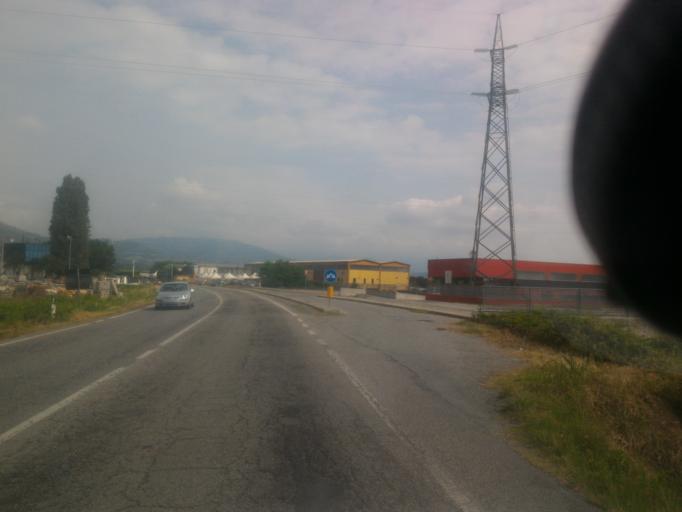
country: IT
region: Piedmont
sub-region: Provincia di Torino
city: Bricherasio
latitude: 44.8272
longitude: 7.3121
